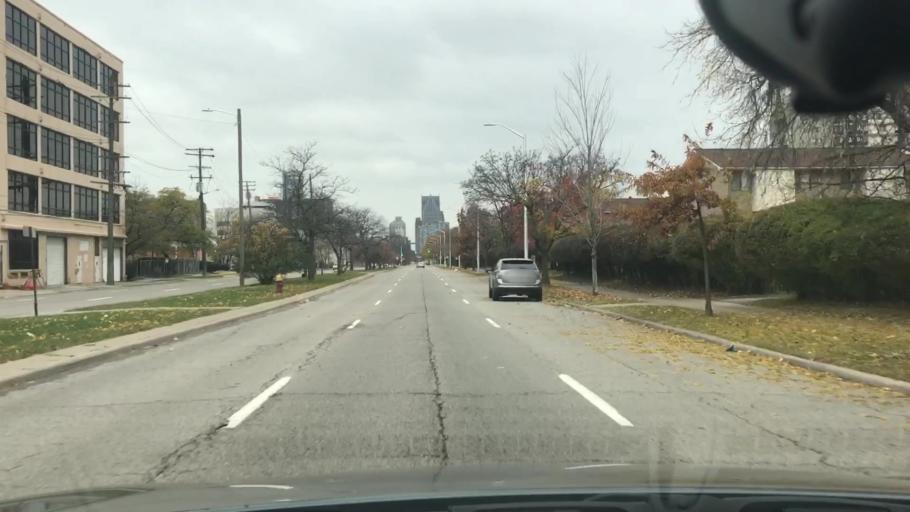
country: US
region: Michigan
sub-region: Wayne County
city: Detroit
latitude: 42.3405
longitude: -83.0201
